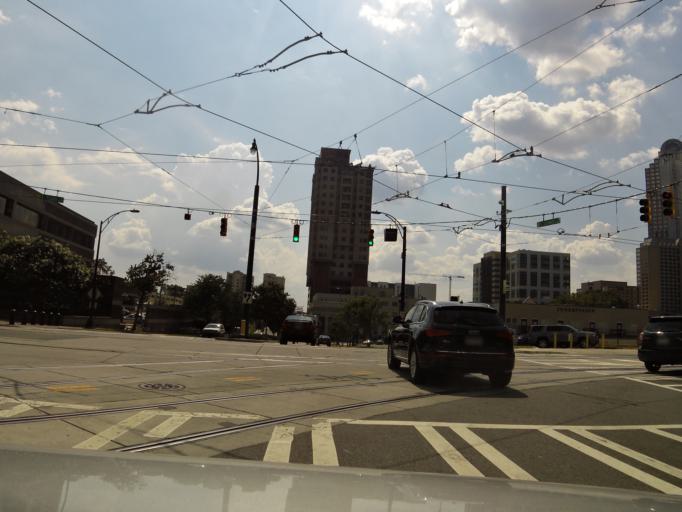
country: US
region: North Carolina
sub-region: Mecklenburg County
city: Charlotte
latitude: 35.2240
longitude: -80.8389
